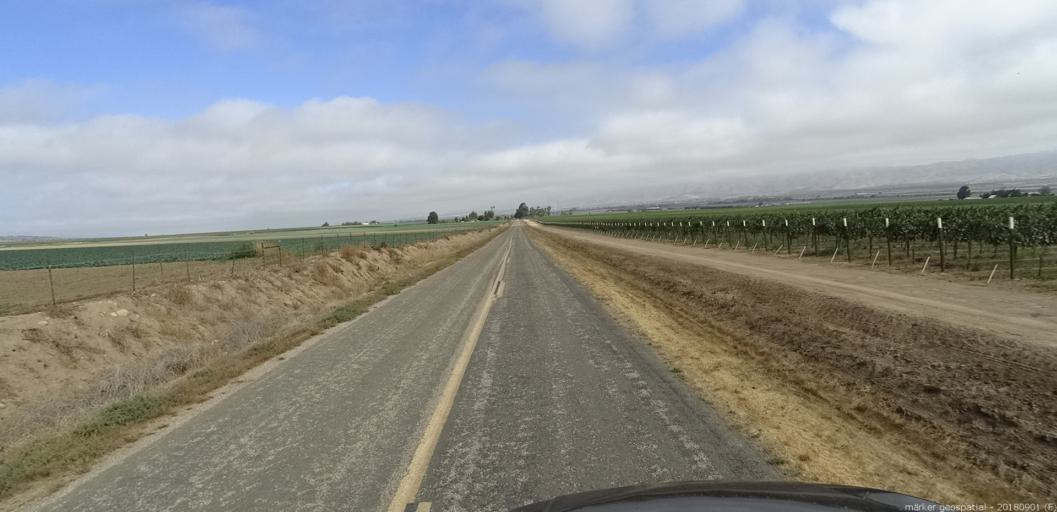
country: US
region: California
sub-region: Monterey County
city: Soledad
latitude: 36.3646
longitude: -121.3356
